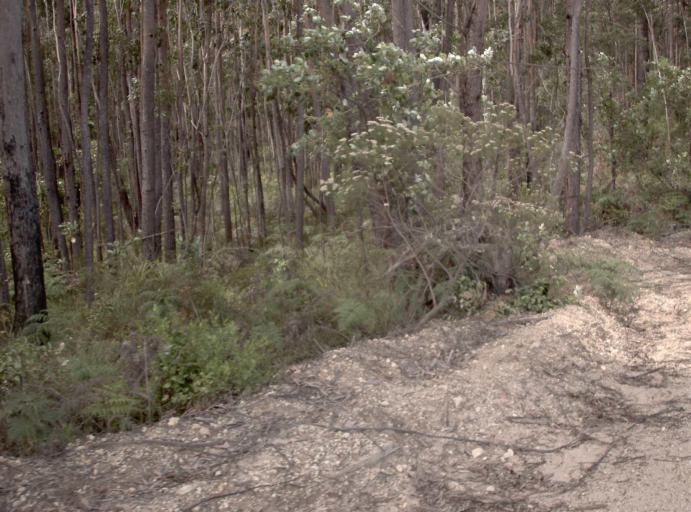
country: AU
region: Victoria
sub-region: East Gippsland
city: Lakes Entrance
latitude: -37.6227
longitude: 148.6795
